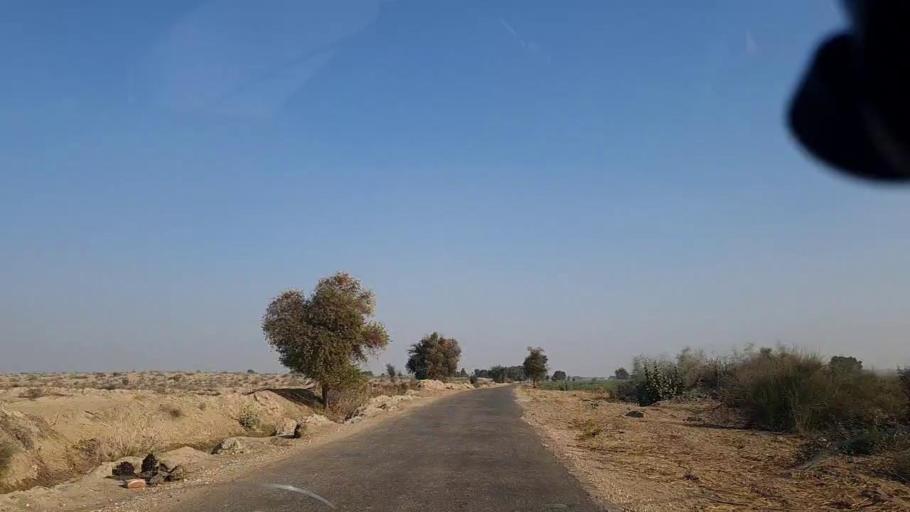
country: PK
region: Sindh
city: Khanpur
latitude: 27.6818
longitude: 69.5529
